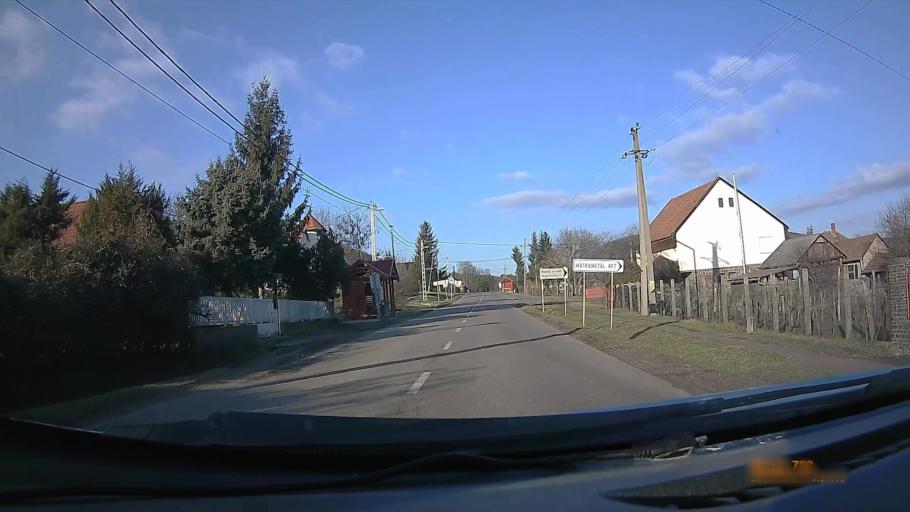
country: HU
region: Heves
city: Sirok
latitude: 47.8996
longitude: 20.1795
